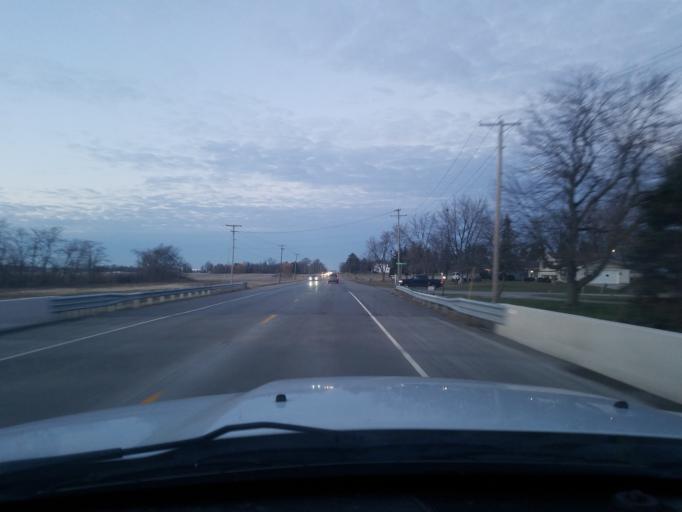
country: US
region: Indiana
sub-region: Wells County
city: Ossian
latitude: 40.9371
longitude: -85.1674
